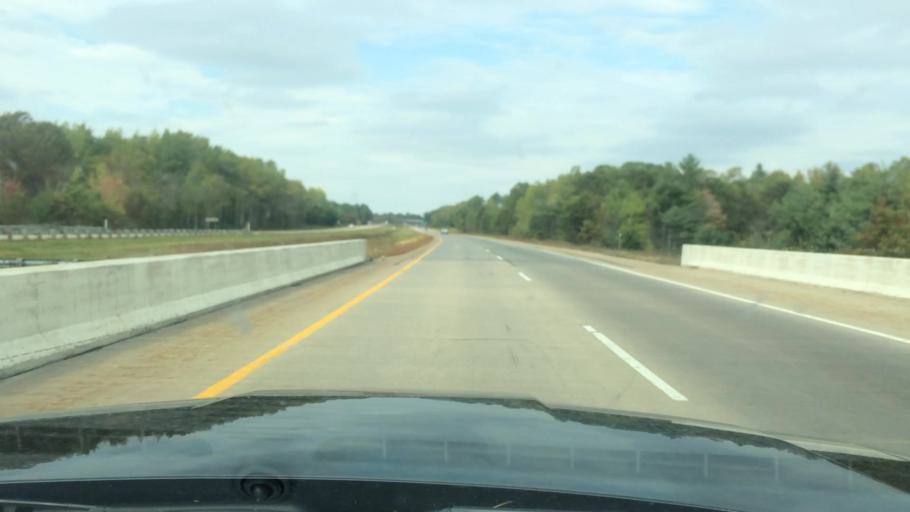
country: US
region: Wisconsin
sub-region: Marathon County
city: Mosinee
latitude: 44.7183
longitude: -89.6644
